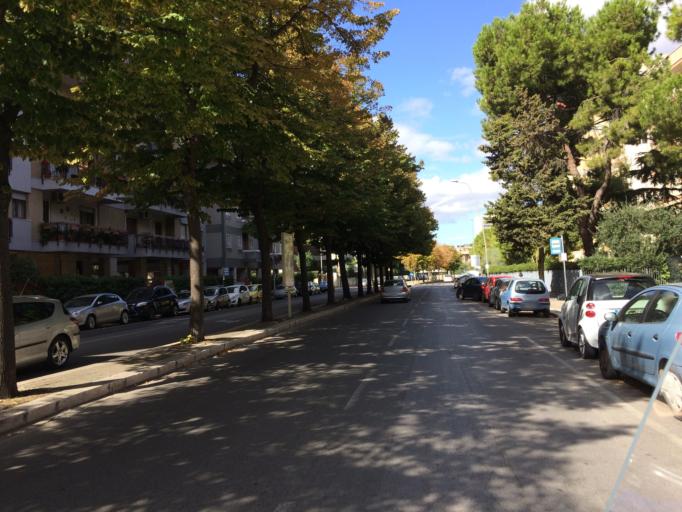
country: IT
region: Apulia
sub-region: Provincia di Bari
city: Bari
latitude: 41.1015
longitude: 16.8592
